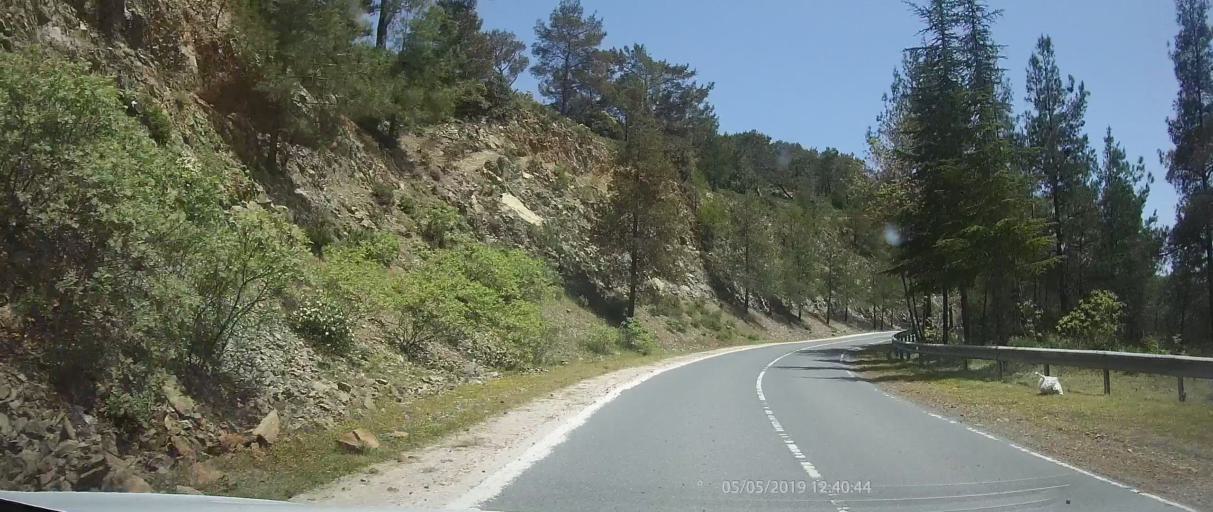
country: CY
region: Lefkosia
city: Kakopetria
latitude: 34.9881
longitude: 32.8025
